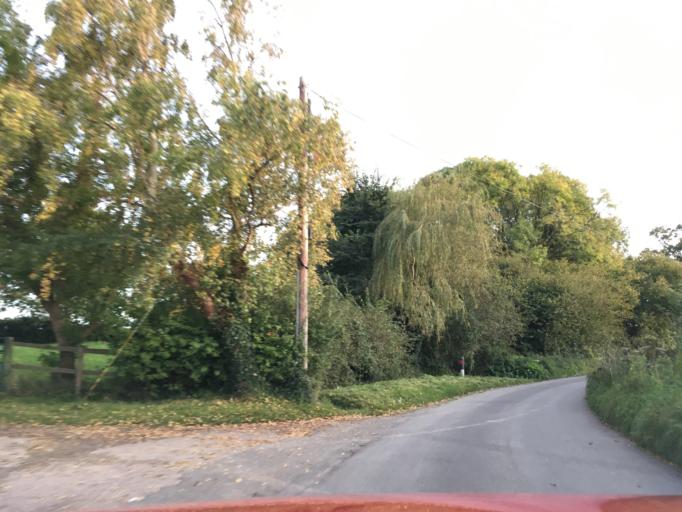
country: GB
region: England
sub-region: South Gloucestershire
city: Thornbury
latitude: 51.6164
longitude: -2.5461
